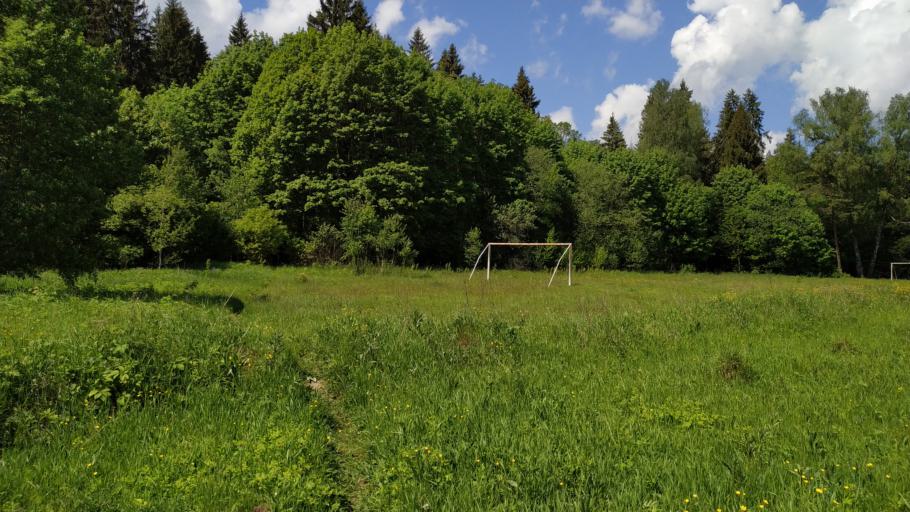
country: RU
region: Moskovskaya
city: Dorokhovo
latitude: 55.6338
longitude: 36.3444
